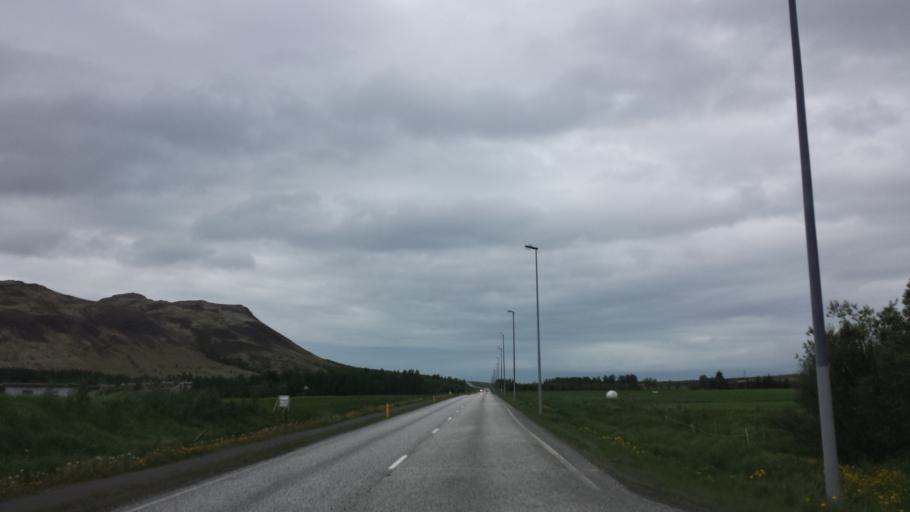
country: IS
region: Capital Region
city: Mosfellsbaer
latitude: 64.1806
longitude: -21.6195
